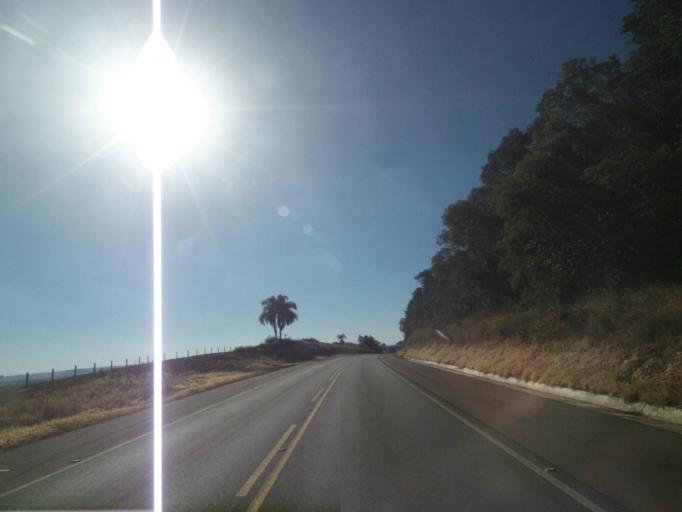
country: BR
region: Parana
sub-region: Tibagi
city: Tibagi
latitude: -24.7107
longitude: -50.4499
